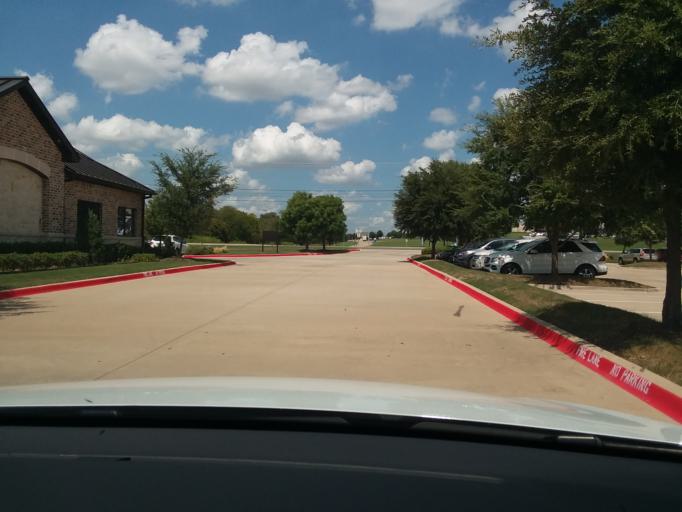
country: US
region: Texas
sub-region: Collin County
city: McKinney
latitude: 33.2175
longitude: -96.6842
